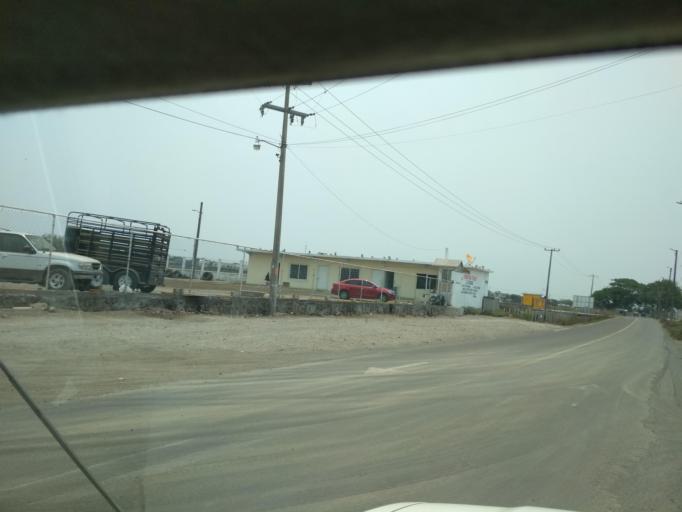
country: MX
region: Veracruz
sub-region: Veracruz
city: Delfino Victoria (Santa Fe)
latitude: 19.2096
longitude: -96.2671
